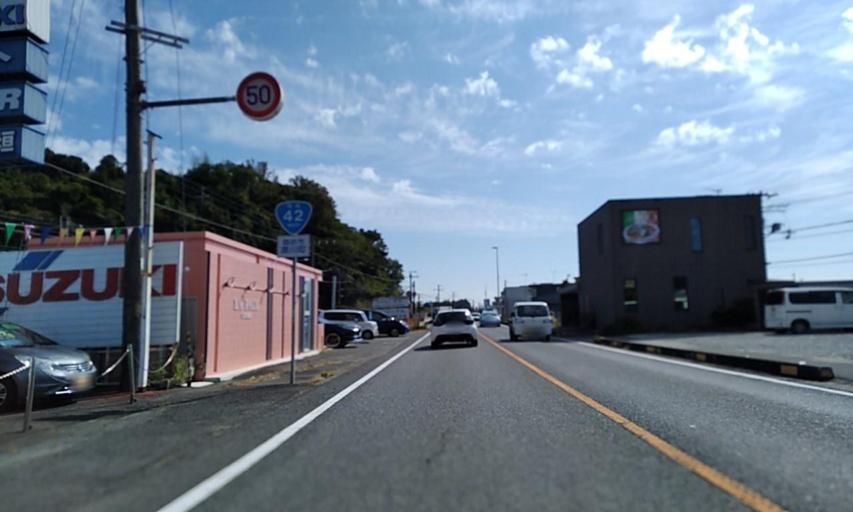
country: JP
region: Wakayama
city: Gobo
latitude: 33.9144
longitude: 135.1485
